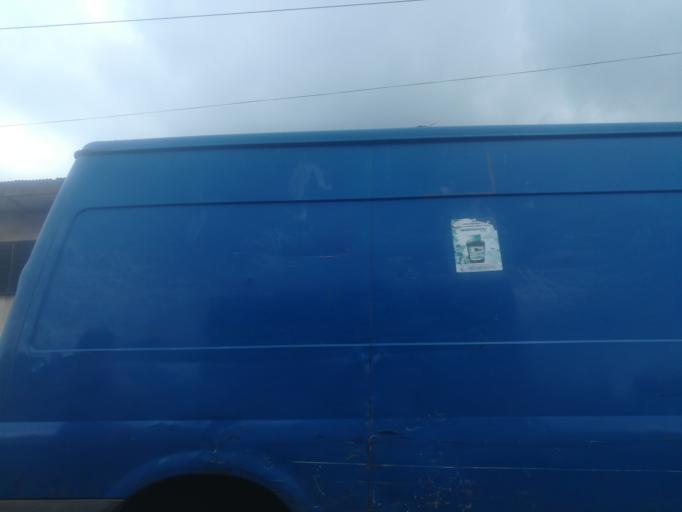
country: NG
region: Lagos
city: Somolu
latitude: 6.5551
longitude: 3.3918
